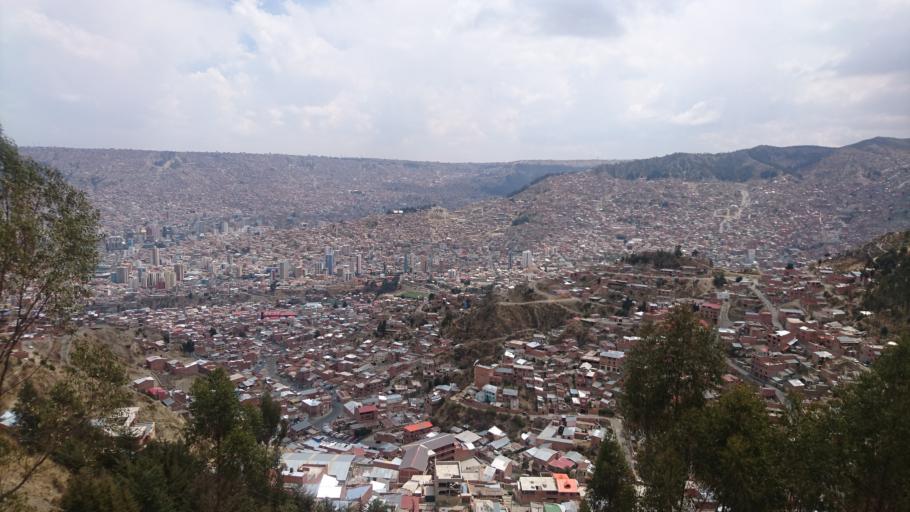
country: BO
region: La Paz
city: La Paz
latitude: -16.4881
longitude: -68.1053
